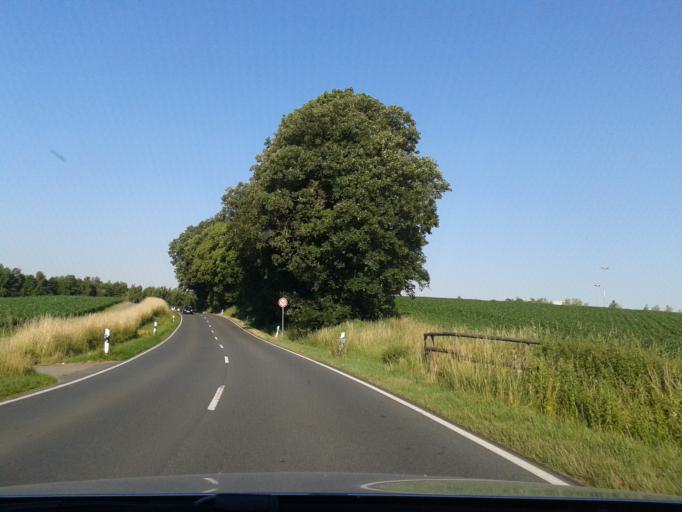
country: DE
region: North Rhine-Westphalia
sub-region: Regierungsbezirk Detmold
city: Lemgo
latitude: 52.0266
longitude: 8.9371
